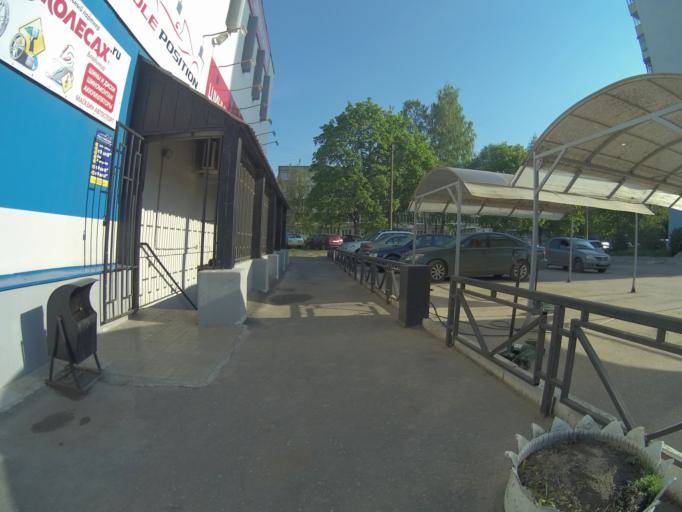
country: RU
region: Vladimir
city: Kommunar
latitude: 56.1734
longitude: 40.4620
